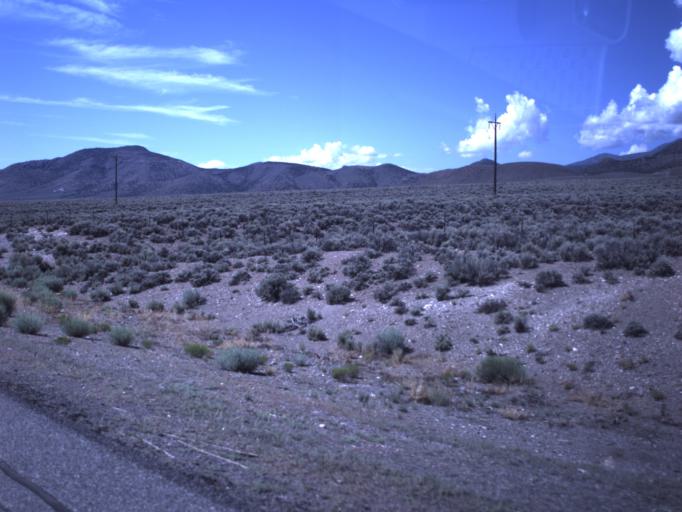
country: US
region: Utah
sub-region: Piute County
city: Junction
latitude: 38.2890
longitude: -112.2253
